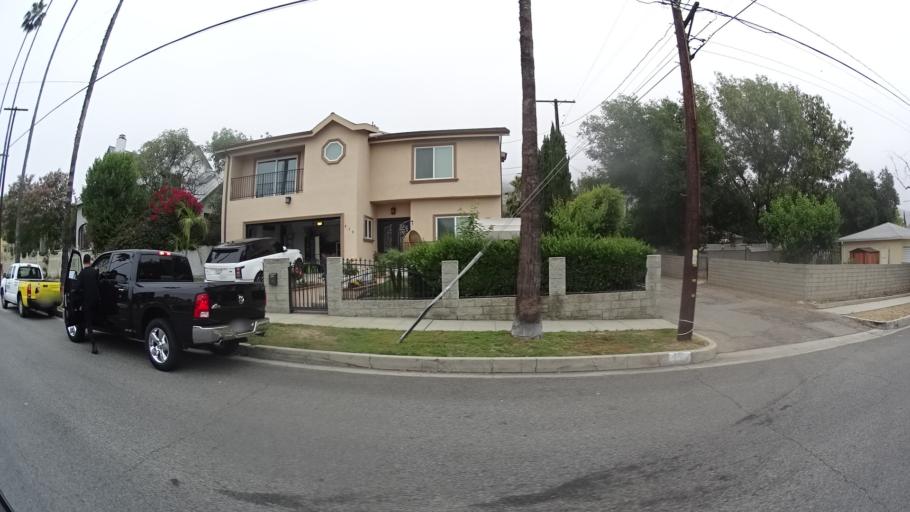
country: US
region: California
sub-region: Los Angeles County
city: Burbank
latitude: 34.1877
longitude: -118.2956
